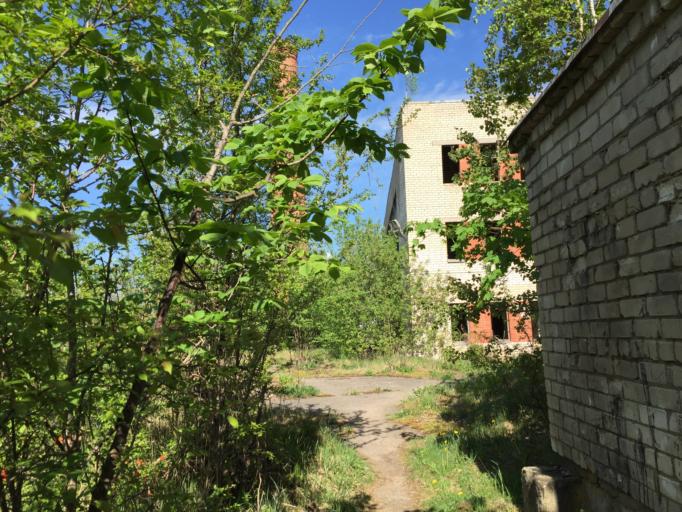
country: LV
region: Bauskas Rajons
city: Bauska
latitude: 56.4150
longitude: 24.1898
